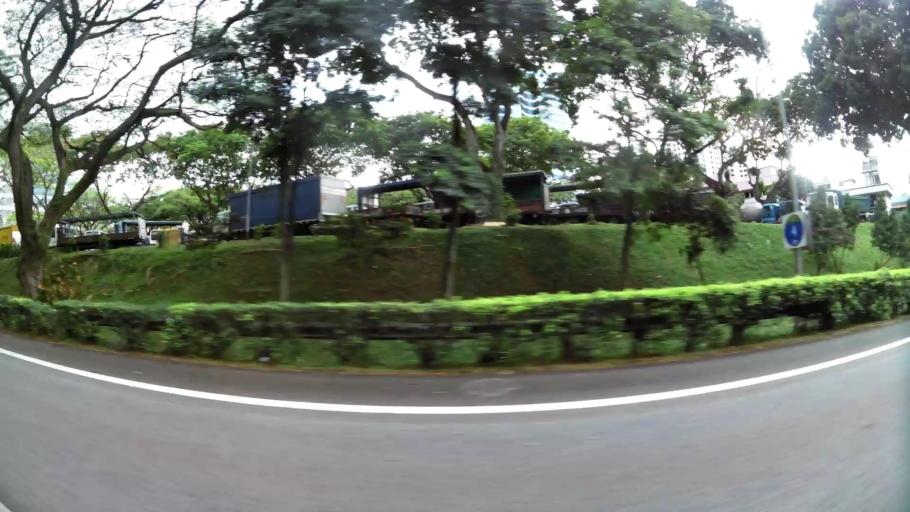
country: SG
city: Singapore
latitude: 1.2819
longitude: 103.8152
